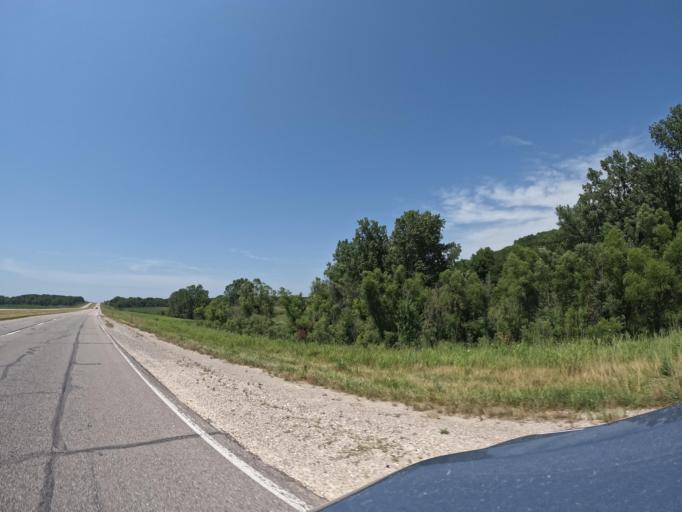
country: US
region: Iowa
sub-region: Henry County
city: Mount Pleasant
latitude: 40.9708
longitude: -91.6423
